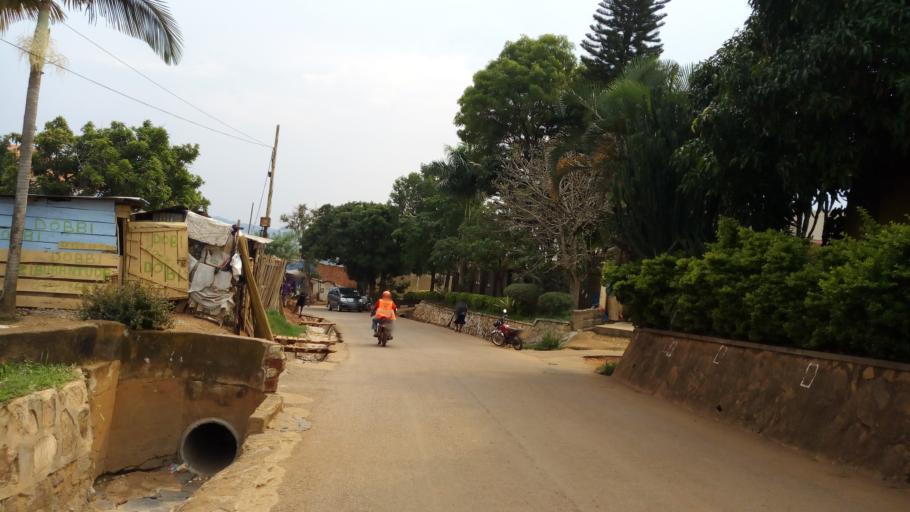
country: UG
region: Central Region
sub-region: Wakiso District
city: Kireka
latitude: 0.3094
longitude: 32.6408
